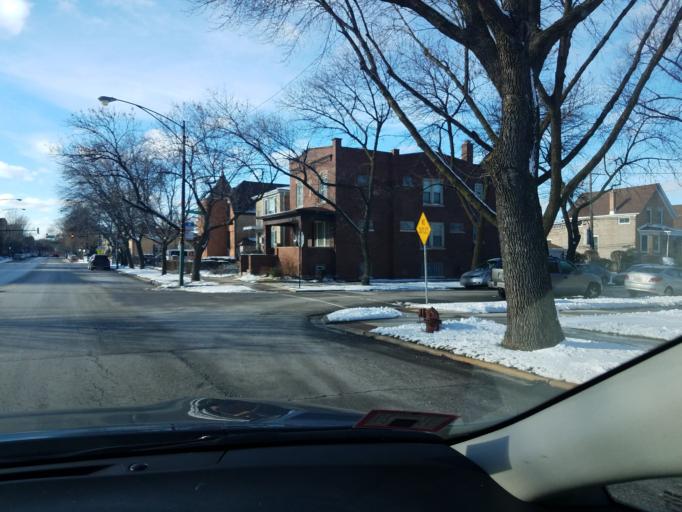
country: US
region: Illinois
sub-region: Cook County
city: Lincolnwood
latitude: 41.9607
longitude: -87.7510
